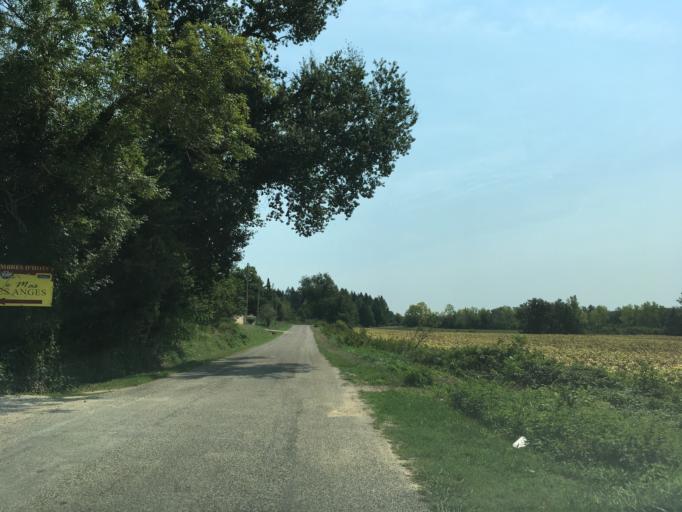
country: FR
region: Midi-Pyrenees
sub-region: Departement du Tarn-et-Garonne
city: Saint-Nauphary
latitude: 43.9839
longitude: 1.4091
